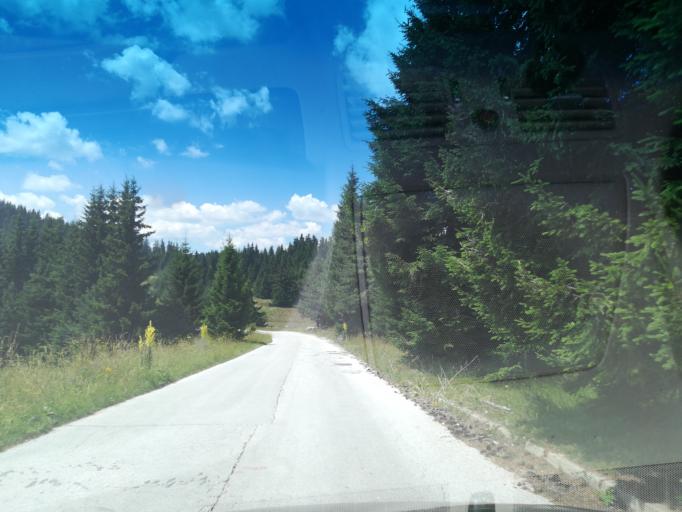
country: BG
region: Smolyan
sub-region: Obshtina Chepelare
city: Chepelare
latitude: 41.6926
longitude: 24.7607
